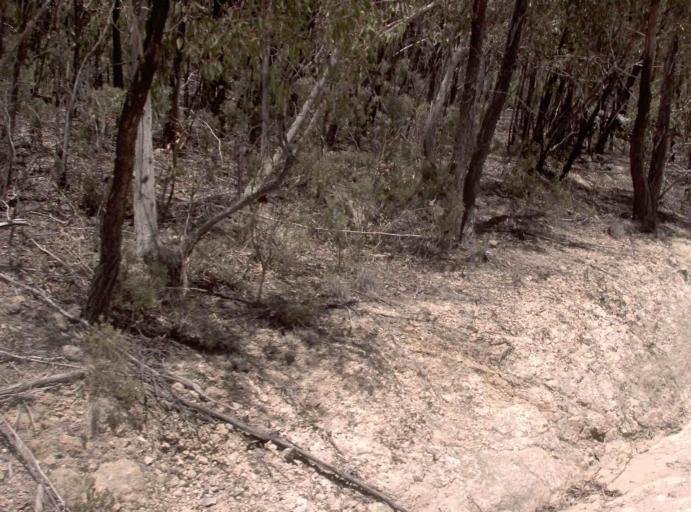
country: AU
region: New South Wales
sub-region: Snowy River
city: Jindabyne
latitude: -37.0845
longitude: 148.3282
